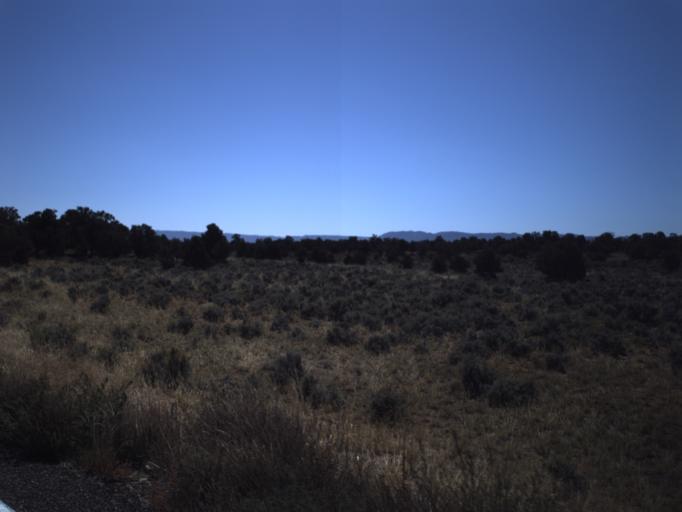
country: US
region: Utah
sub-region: Wayne County
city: Loa
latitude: 37.8530
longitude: -111.4316
